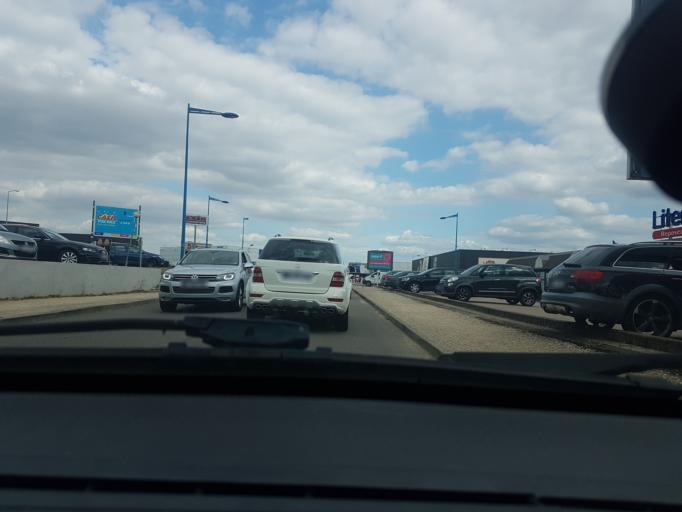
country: FR
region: Bourgogne
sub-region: Departement de la Cote-d'Or
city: Sennecey-les-Dijon
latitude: 47.3103
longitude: 5.0945
